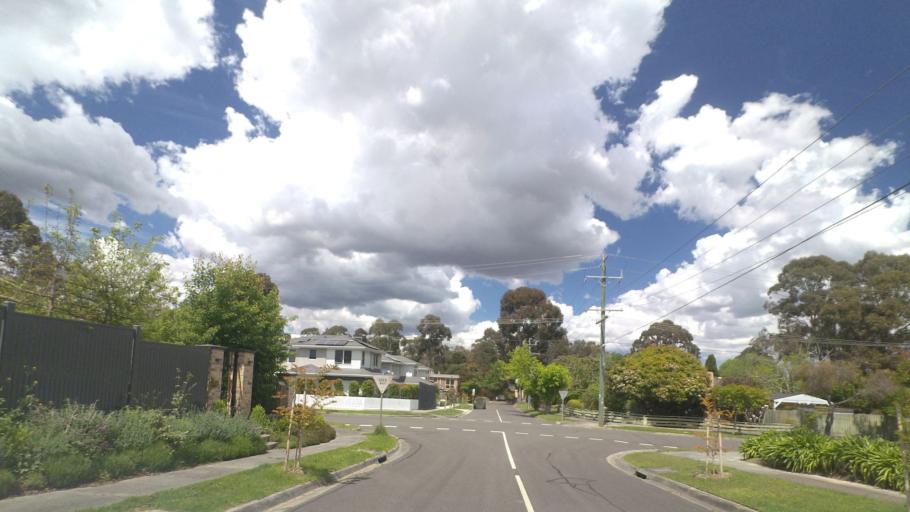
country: AU
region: Victoria
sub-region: Maroondah
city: Croydon South
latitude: -37.8077
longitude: 145.2744
